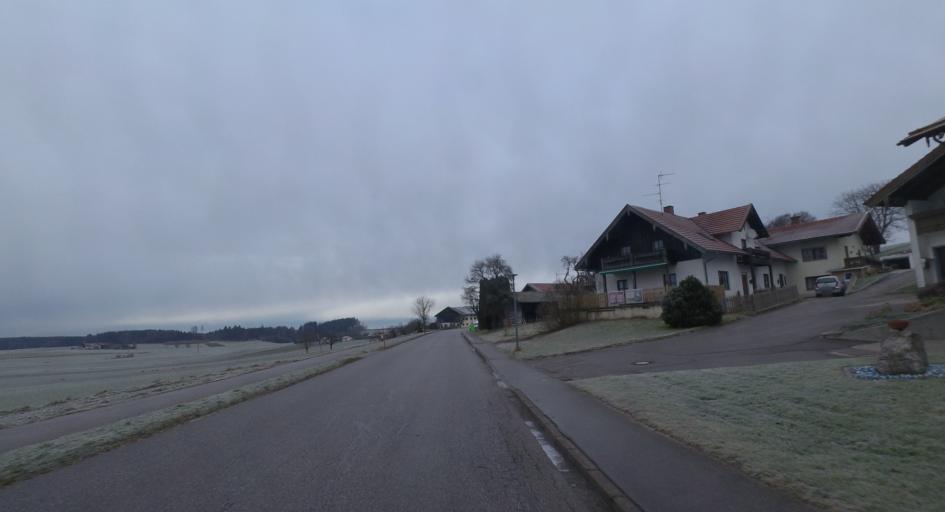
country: DE
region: Bavaria
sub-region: Upper Bavaria
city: Traunstein
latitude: 47.9086
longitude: 12.6501
